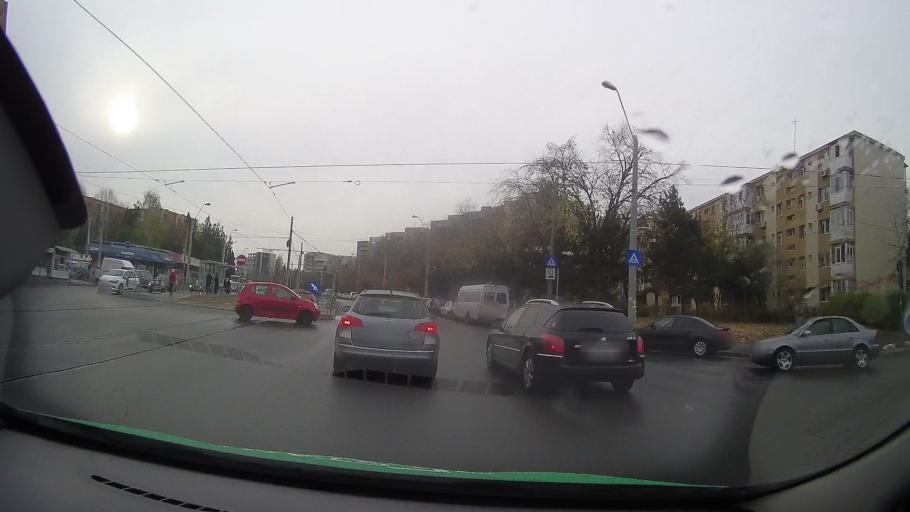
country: RO
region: Prahova
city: Ploiesti
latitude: 44.9317
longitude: 25.9890
